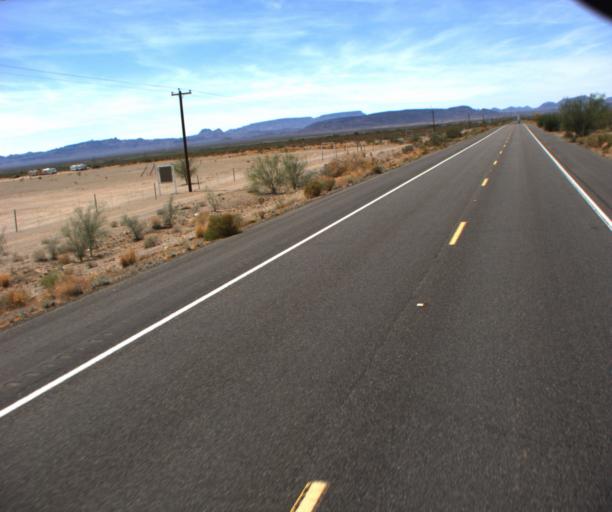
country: US
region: Arizona
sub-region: La Paz County
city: Salome
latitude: 33.7169
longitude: -113.7793
